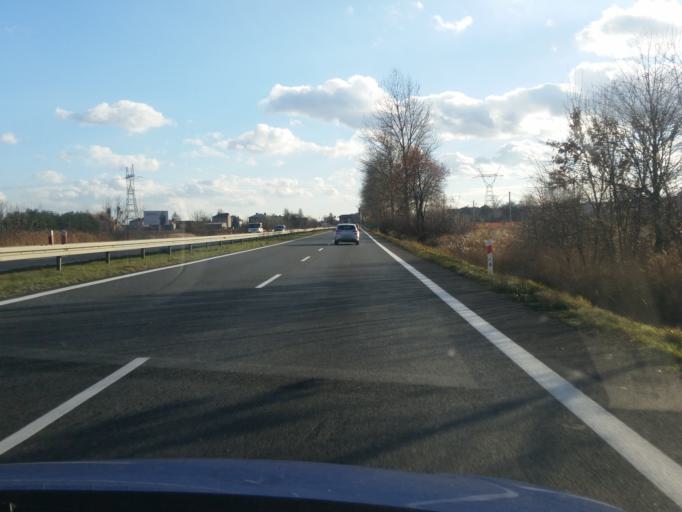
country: PL
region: Silesian Voivodeship
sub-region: Powiat bedzinski
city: Siewierz
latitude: 50.5106
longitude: 19.1957
